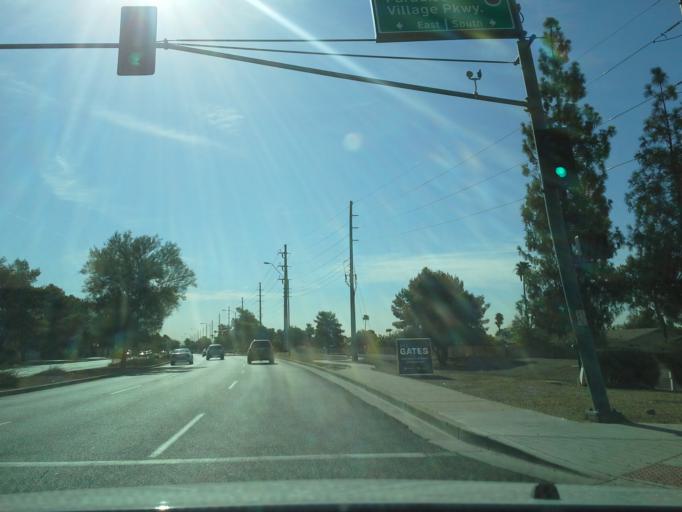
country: US
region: Arizona
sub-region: Maricopa County
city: Paradise Valley
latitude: 33.5972
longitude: -111.9758
